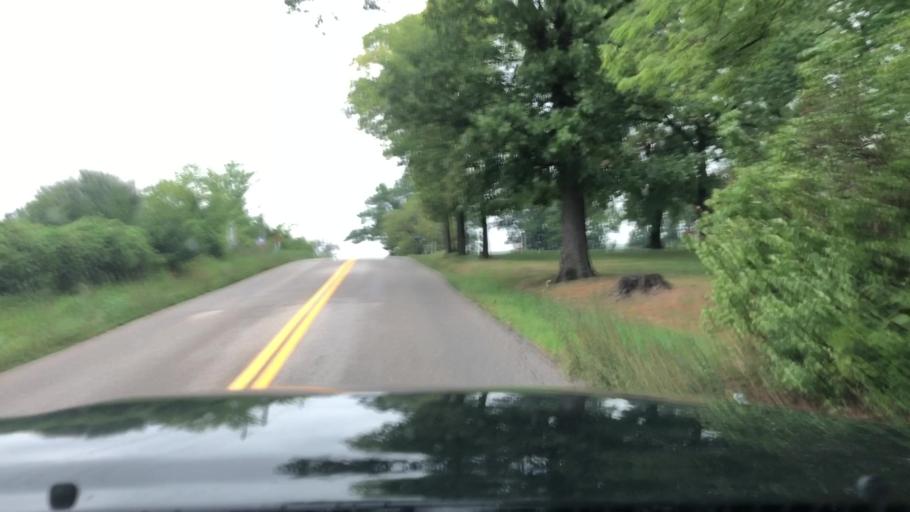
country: US
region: Missouri
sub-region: Saint Charles County
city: Wentzville
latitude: 38.8417
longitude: -90.8876
